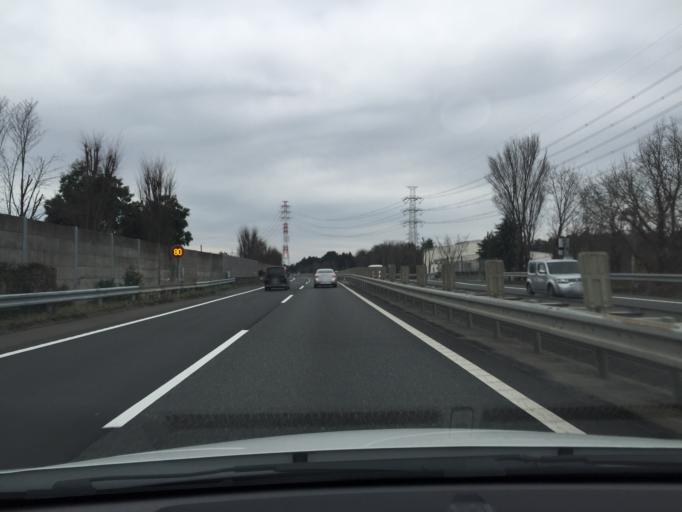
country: JP
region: Saitama
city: Sayama
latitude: 35.8972
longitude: 139.3888
